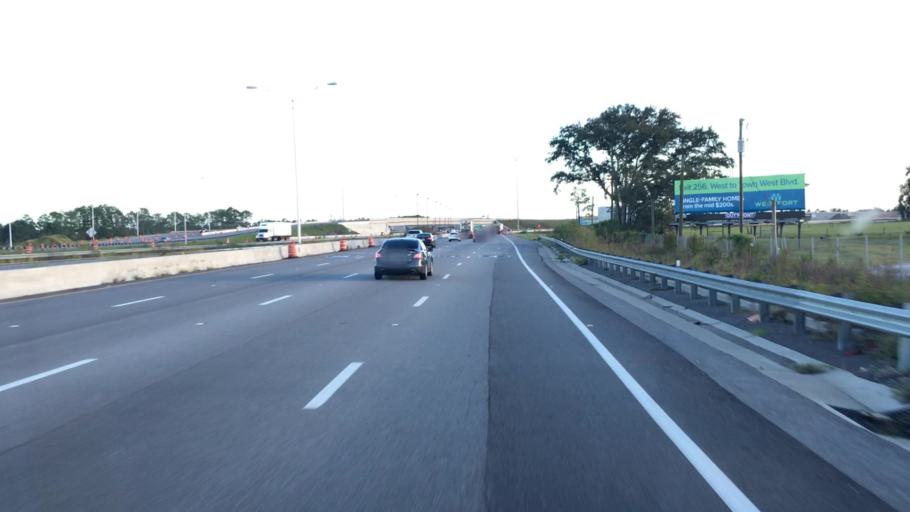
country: US
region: Florida
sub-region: Volusia County
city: Daytona Beach
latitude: 29.1618
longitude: -81.0797
